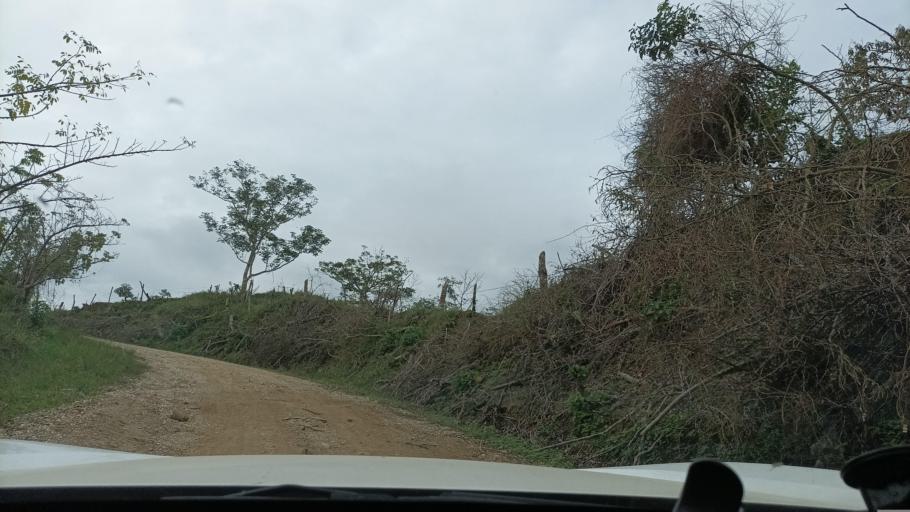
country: MX
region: Veracruz
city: Hidalgotitlan
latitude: 17.5833
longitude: -94.4229
